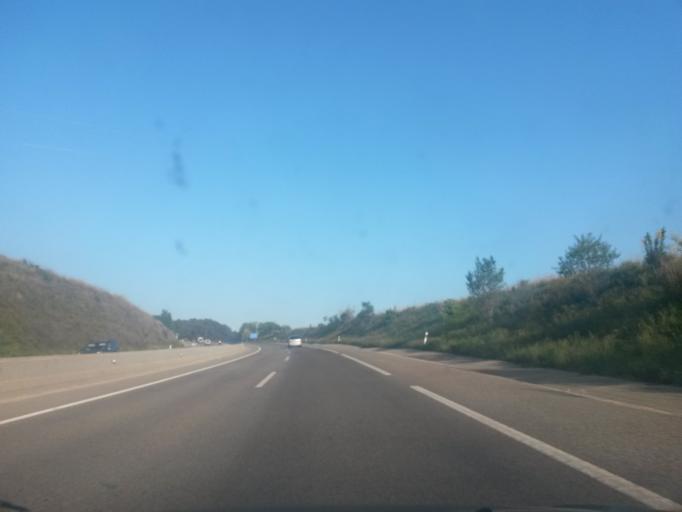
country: ES
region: Catalonia
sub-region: Provincia de Girona
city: Sant Ferriol
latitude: 42.2121
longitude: 2.6647
